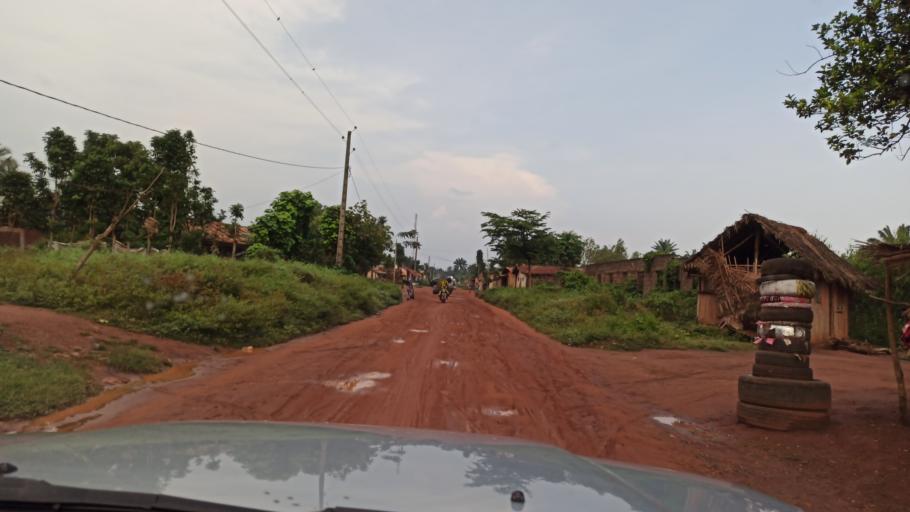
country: BJ
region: Queme
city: Porto-Novo
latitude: 6.4949
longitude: 2.6919
